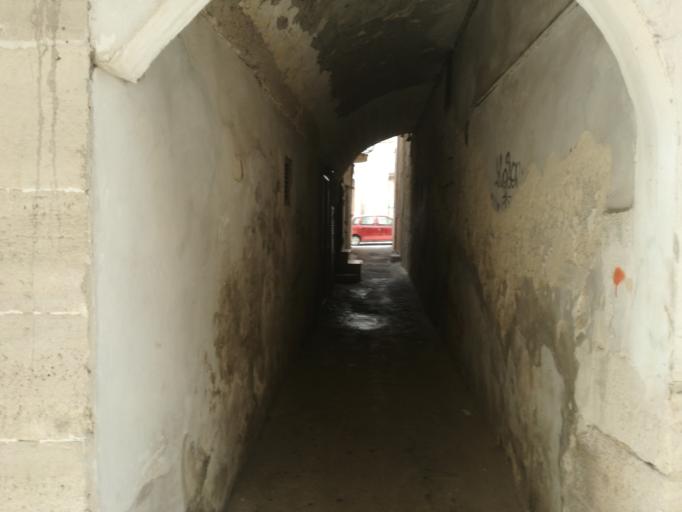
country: IT
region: Apulia
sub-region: Provincia di Bari
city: Triggiano
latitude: 41.0639
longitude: 16.9233
